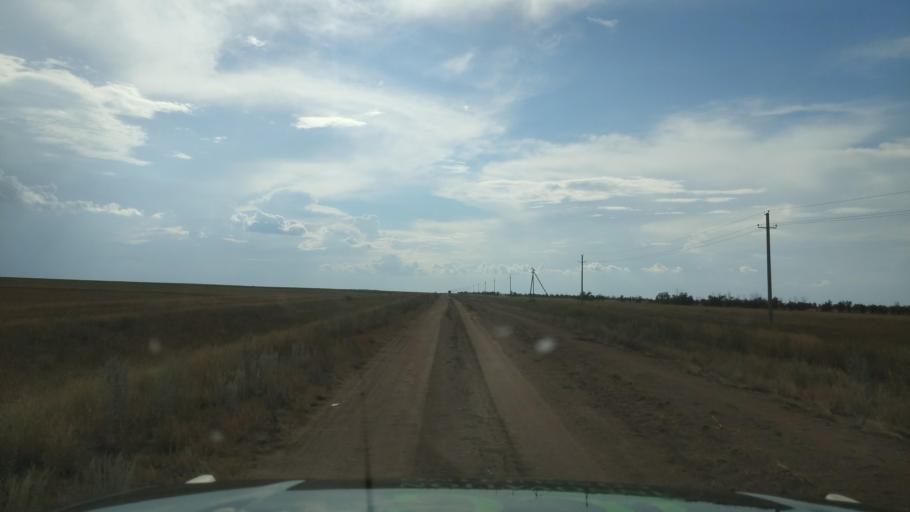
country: KZ
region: Pavlodar
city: Pavlodar
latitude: 52.5125
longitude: 77.5031
